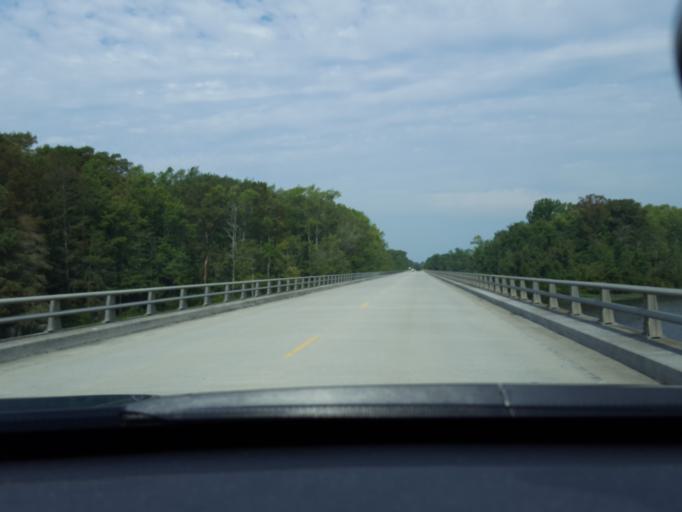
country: US
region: North Carolina
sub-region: Washington County
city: Plymouth
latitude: 35.9203
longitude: -76.7292
